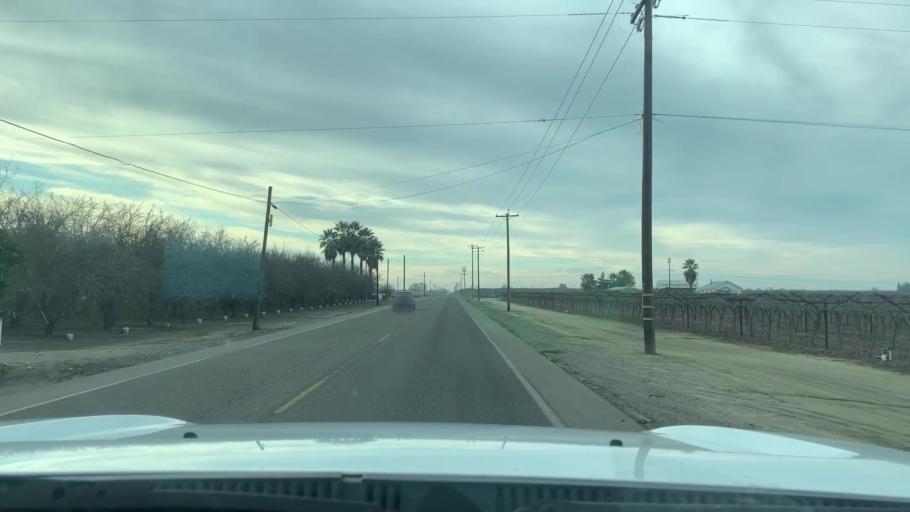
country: US
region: California
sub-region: Fresno County
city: Easton
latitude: 36.6054
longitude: -119.7615
